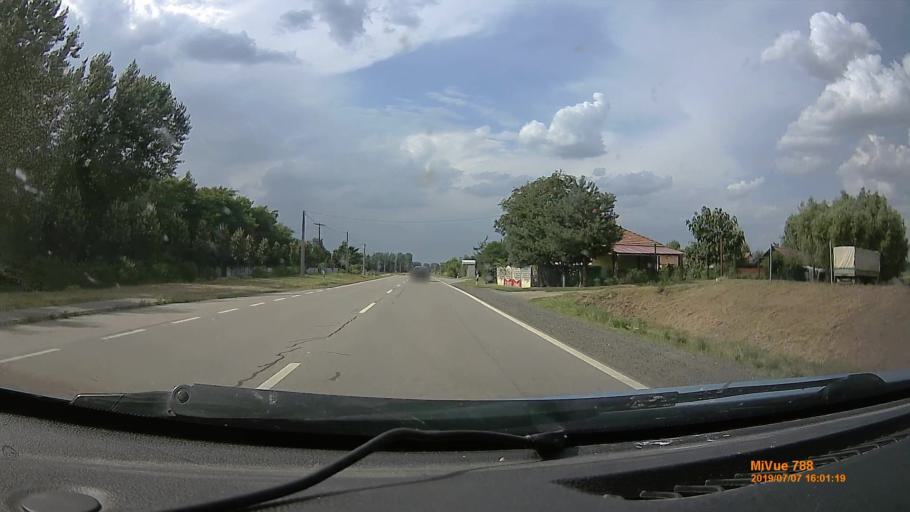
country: HU
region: Heves
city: Boldog
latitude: 47.6089
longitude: 19.7391
